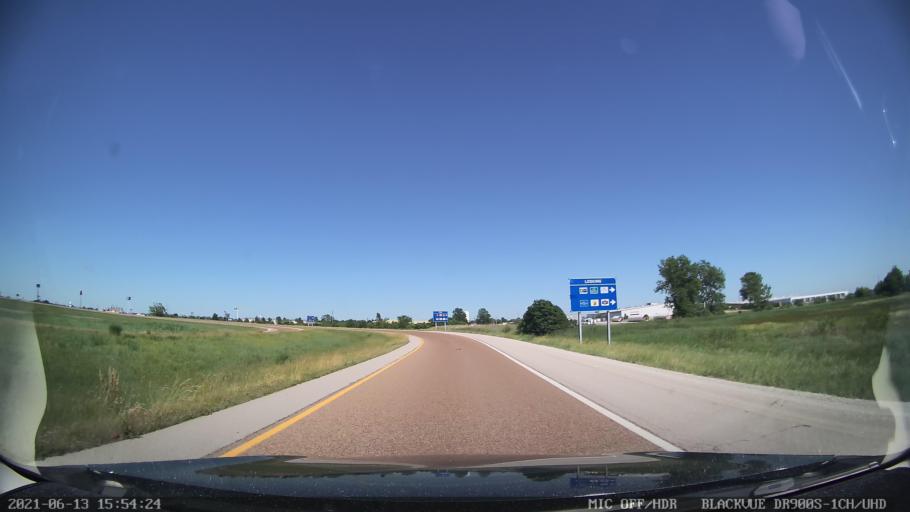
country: US
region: Illinois
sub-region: Montgomery County
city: Litchfield
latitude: 39.1727
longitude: -89.6804
